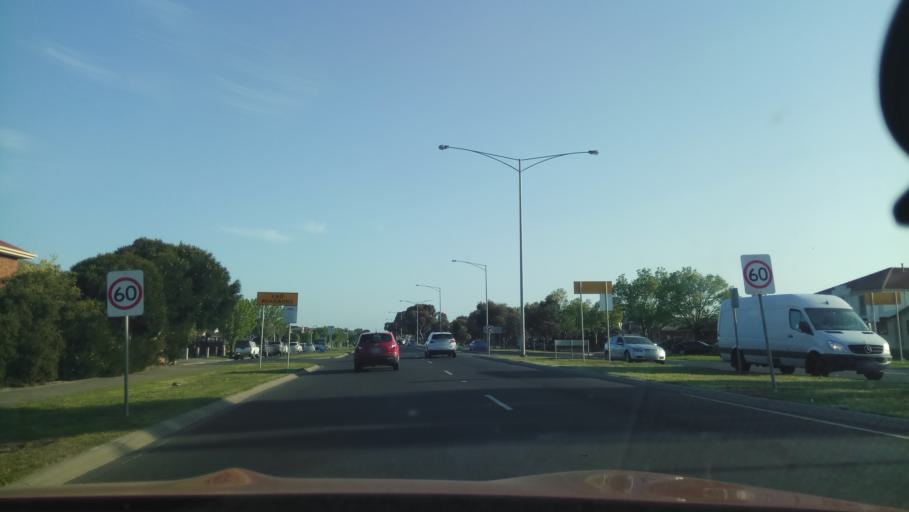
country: AU
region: Victoria
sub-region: Wyndham
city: Point Cook
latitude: -37.8876
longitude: 144.7560
